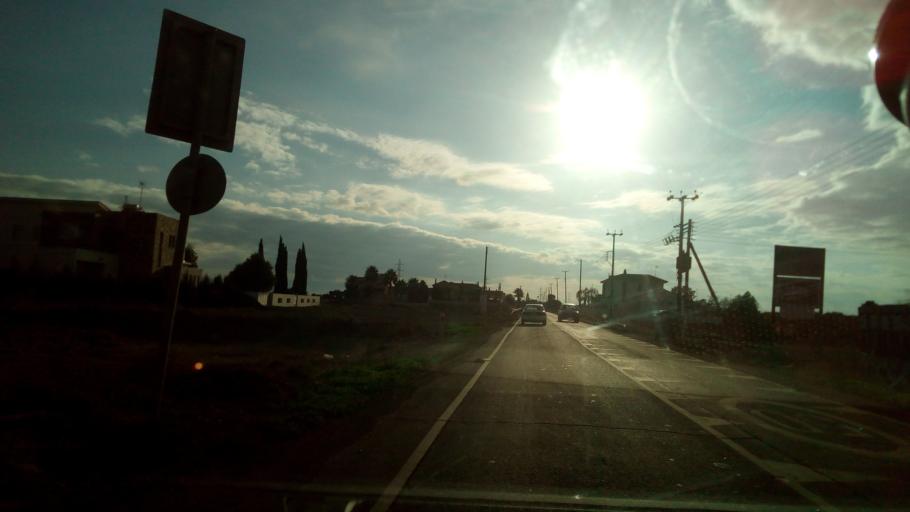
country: CY
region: Ammochostos
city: Avgorou
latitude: 35.0242
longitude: 33.8339
